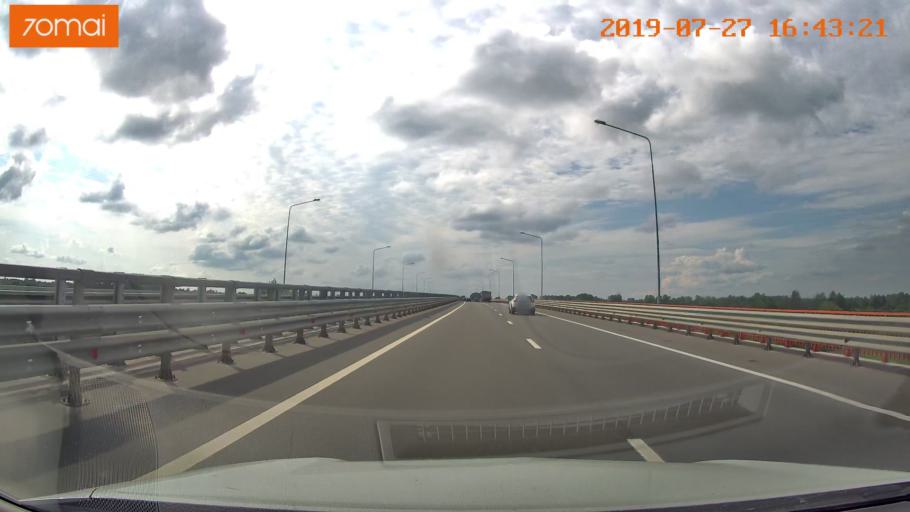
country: RU
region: Kaliningrad
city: Gvardeysk
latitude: 54.6709
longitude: 21.1043
